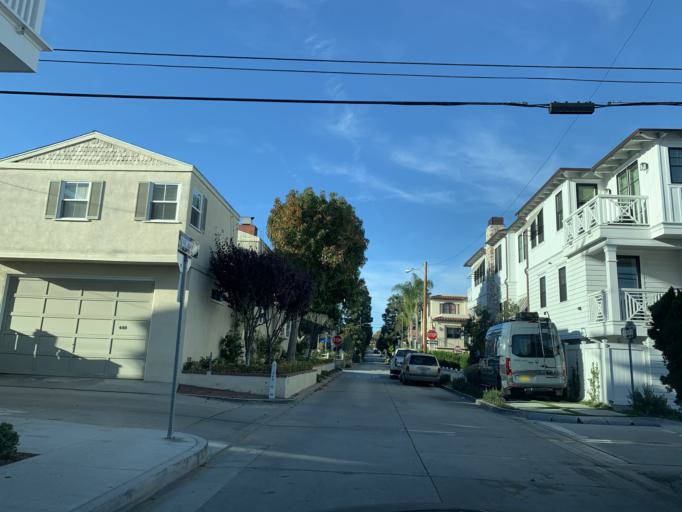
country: US
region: California
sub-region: Los Angeles County
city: Manhattan Beach
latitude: 33.8803
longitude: -118.4047
